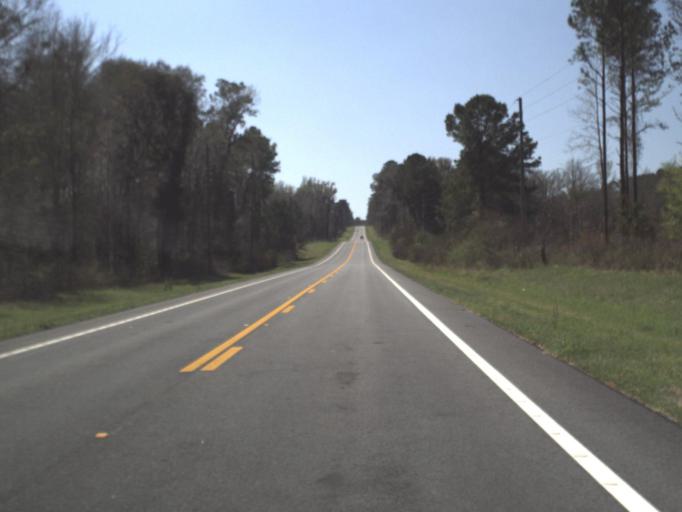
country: US
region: Florida
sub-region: Jefferson County
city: Monticello
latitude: 30.4226
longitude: -84.0201
